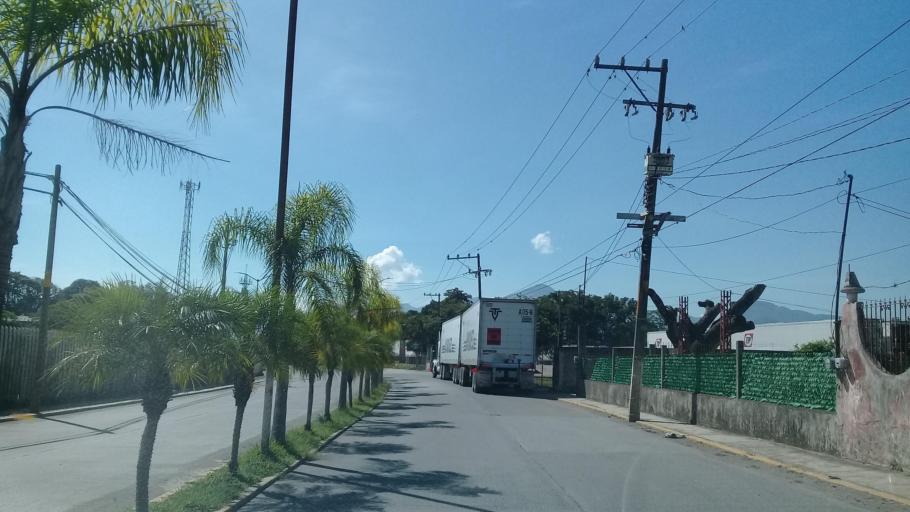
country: MX
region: Veracruz
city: Amatlan de los Reyes
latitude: 18.8556
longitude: -96.9124
